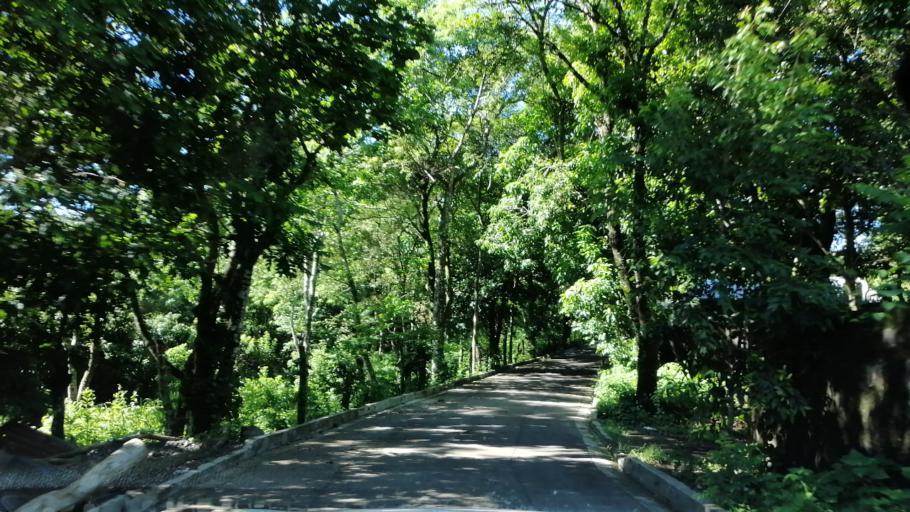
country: SV
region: Morazan
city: Corinto
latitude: 13.8070
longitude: -87.9717
